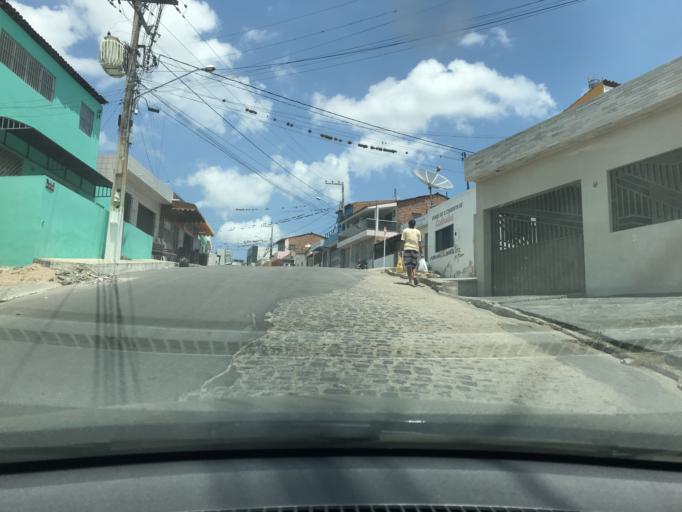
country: BR
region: Pernambuco
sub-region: Bezerros
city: Bezerros
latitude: -8.2341
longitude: -35.7496
